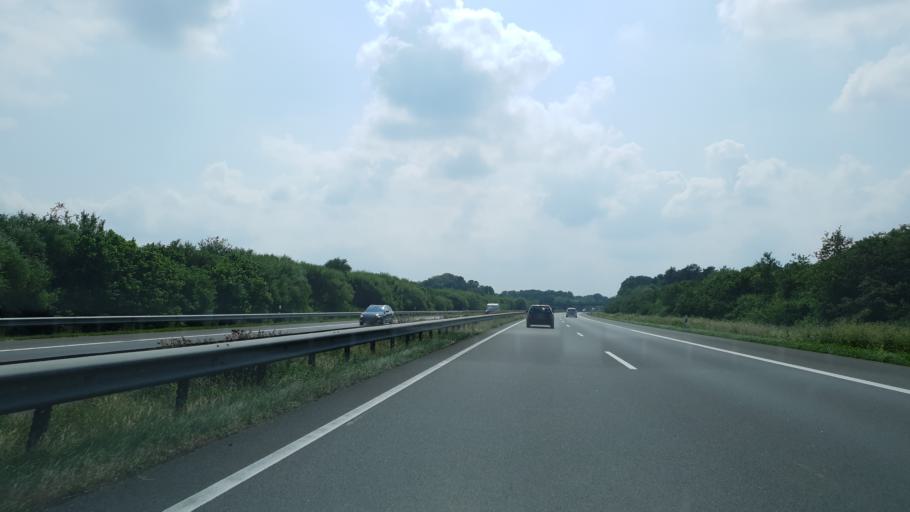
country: DE
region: Lower Saxony
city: Suddendorf
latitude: 52.2935
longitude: 7.2392
